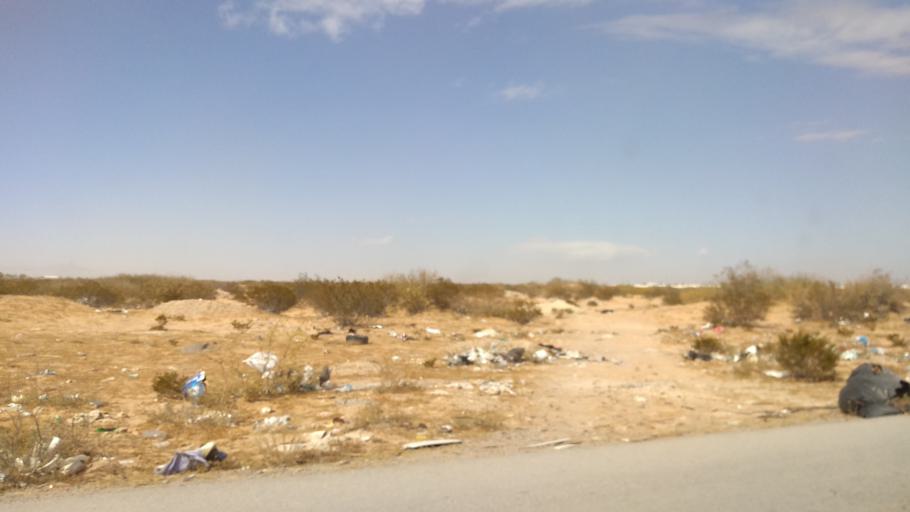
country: US
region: Texas
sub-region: El Paso County
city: San Elizario
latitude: 31.5720
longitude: -106.3317
